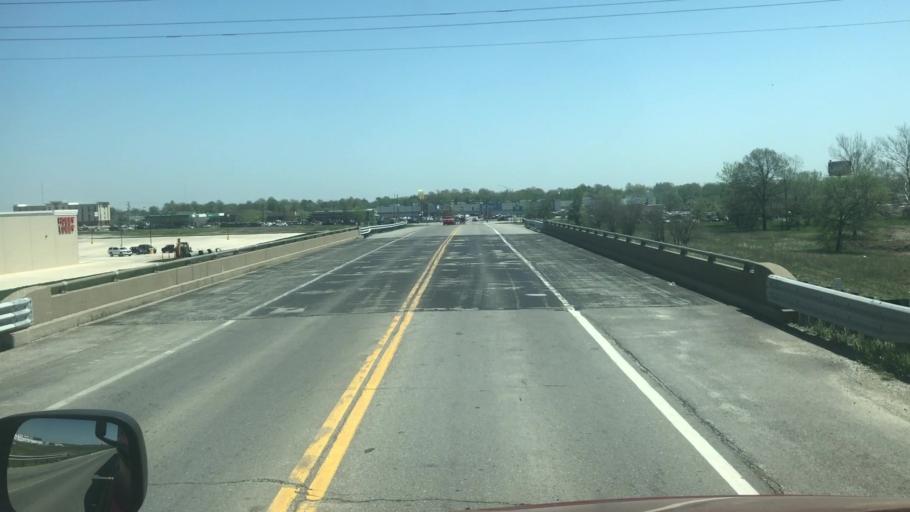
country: US
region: Missouri
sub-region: Adair County
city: Kirksville
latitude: 40.2166
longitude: -92.5867
